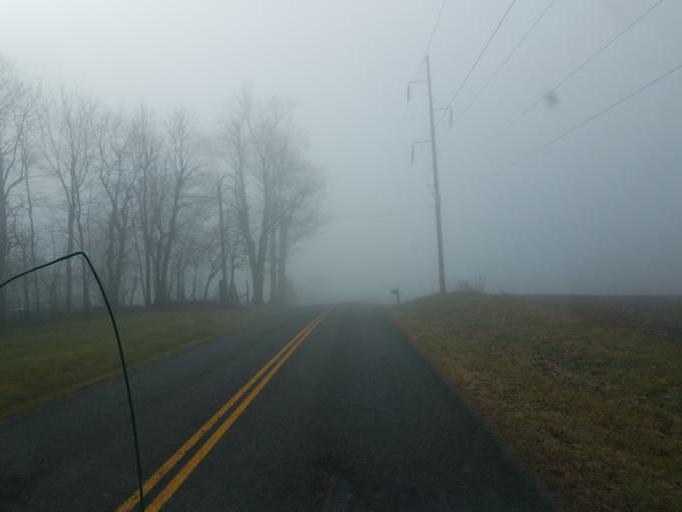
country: US
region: Ohio
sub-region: Champaign County
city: North Lewisburg
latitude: 40.3018
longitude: -83.6269
